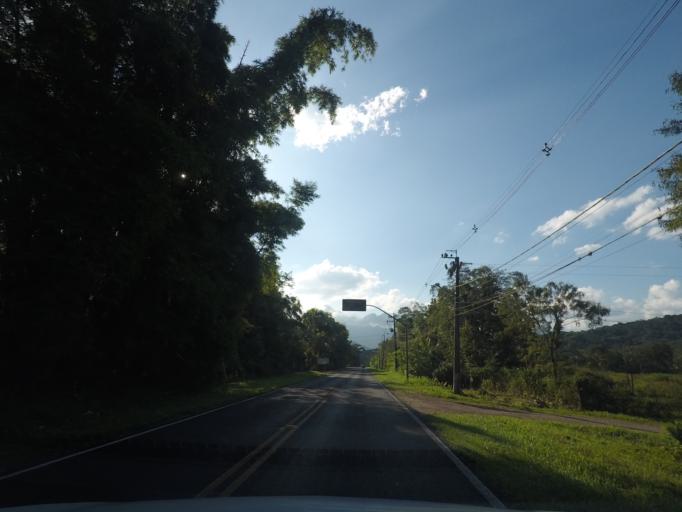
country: BR
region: Parana
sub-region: Antonina
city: Antonina
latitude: -25.4333
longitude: -48.8727
